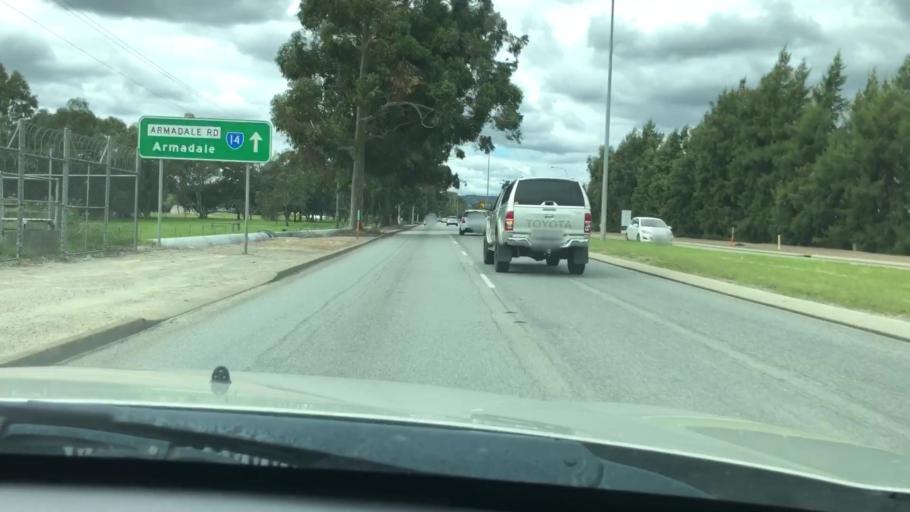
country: AU
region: Western Australia
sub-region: Armadale
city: Seville Grove
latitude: -32.1471
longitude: 115.9751
